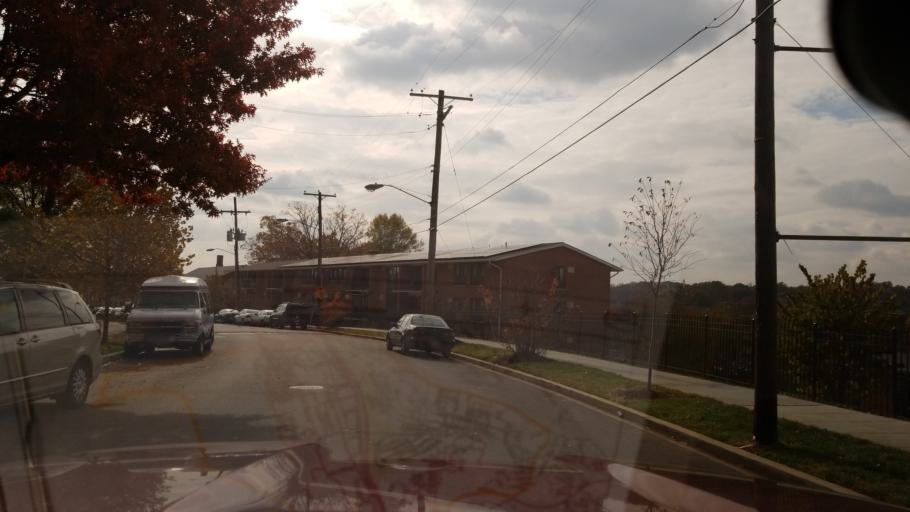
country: US
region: Maryland
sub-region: Prince George's County
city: Glassmanor
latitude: 38.8276
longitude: -77.0024
